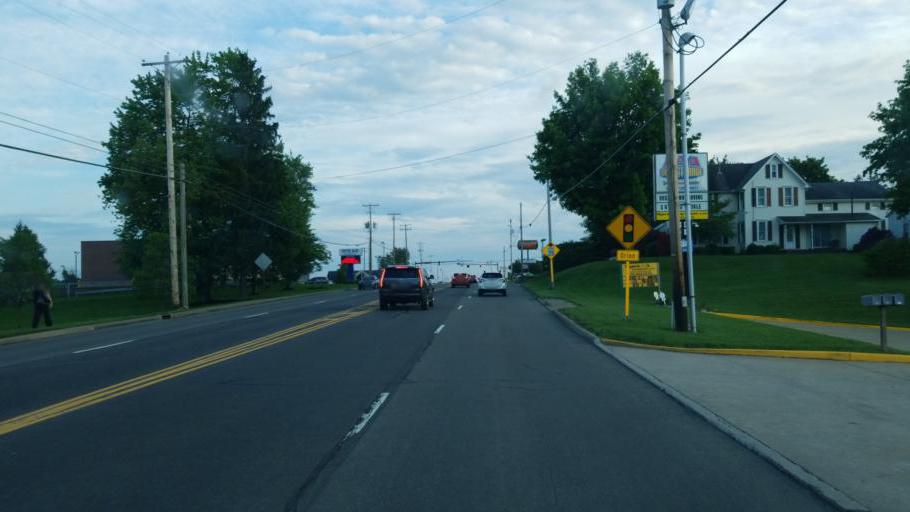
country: US
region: Ohio
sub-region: Stark County
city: North Canton
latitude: 40.9001
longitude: -81.4061
